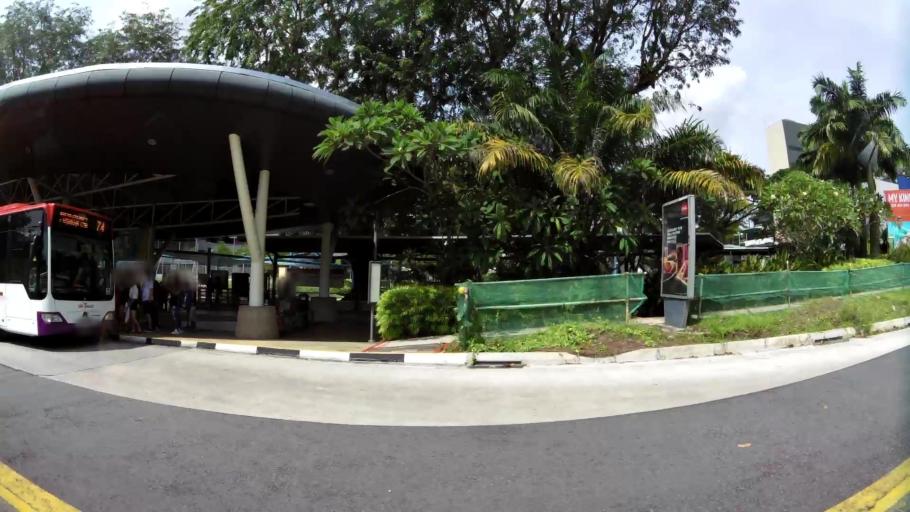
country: SG
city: Singapore
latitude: 1.3326
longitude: 103.7778
